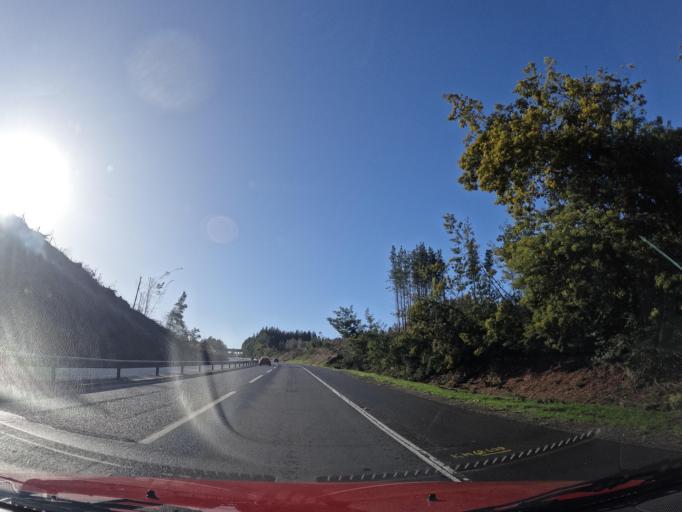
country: CL
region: Biobio
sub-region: Provincia de Concepcion
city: Penco
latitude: -36.7609
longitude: -72.9393
